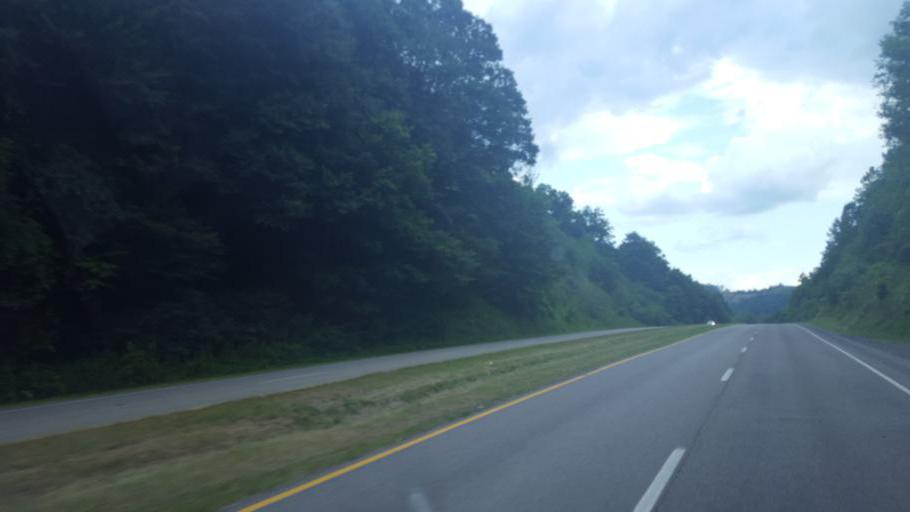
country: US
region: Virginia
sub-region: Wise County
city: Pound
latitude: 37.1236
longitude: -82.6208
